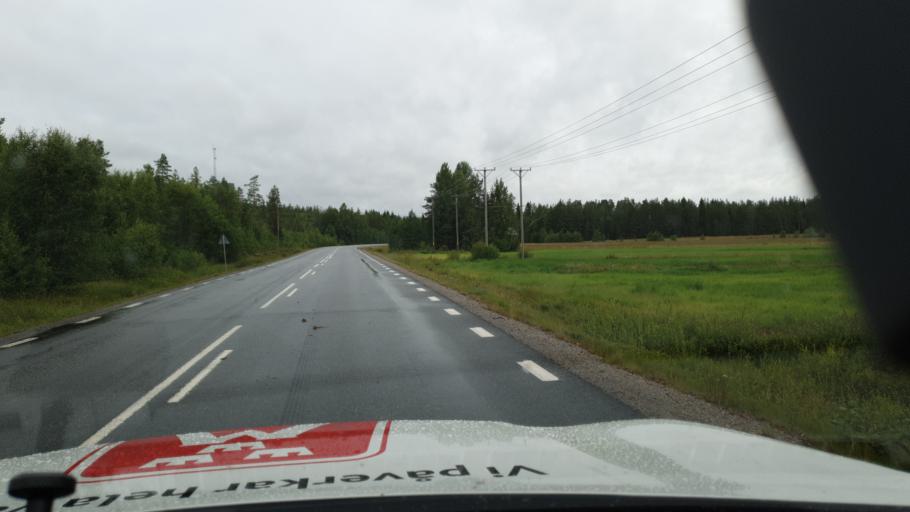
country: SE
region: Vaesterbotten
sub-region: Umea Kommun
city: Saevar
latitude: 63.9019
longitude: 20.5278
